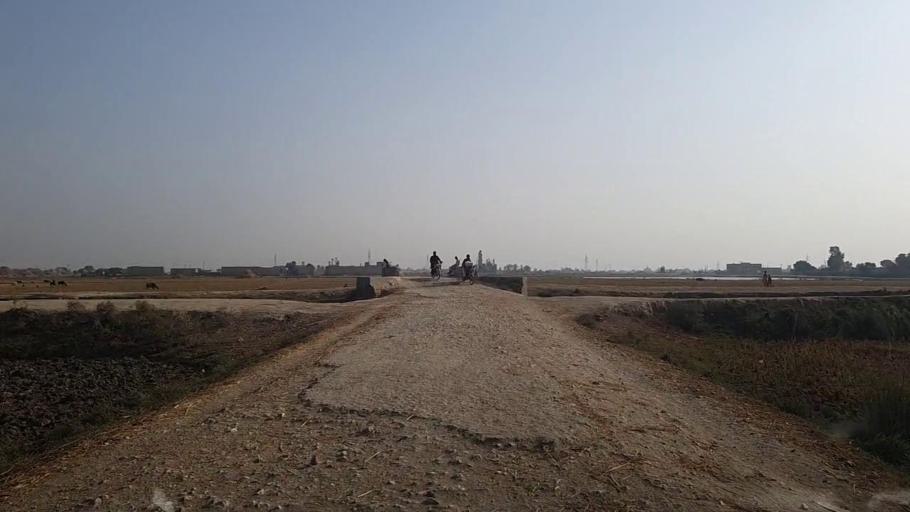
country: PK
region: Sindh
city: Kandhkot
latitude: 28.2807
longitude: 69.2563
